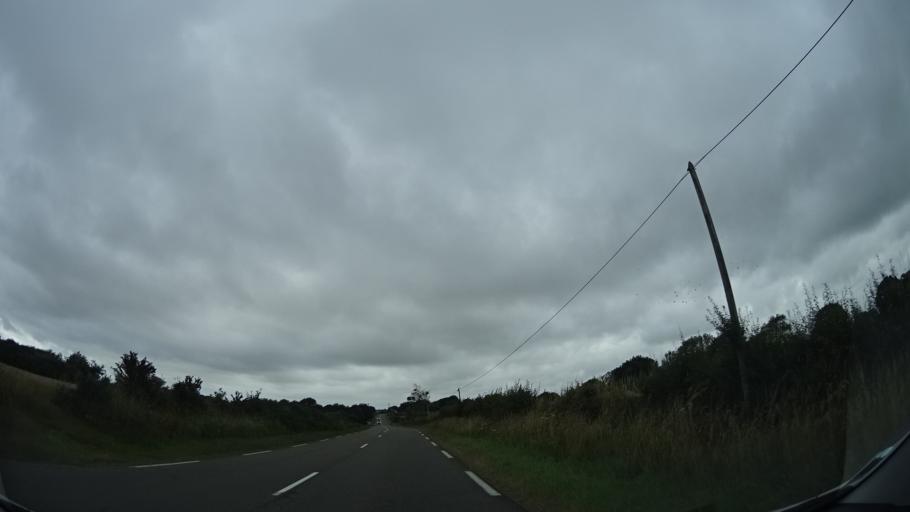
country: FR
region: Lower Normandy
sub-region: Departement de la Manche
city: La Haye-du-Puits
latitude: 49.3142
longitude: -1.6111
